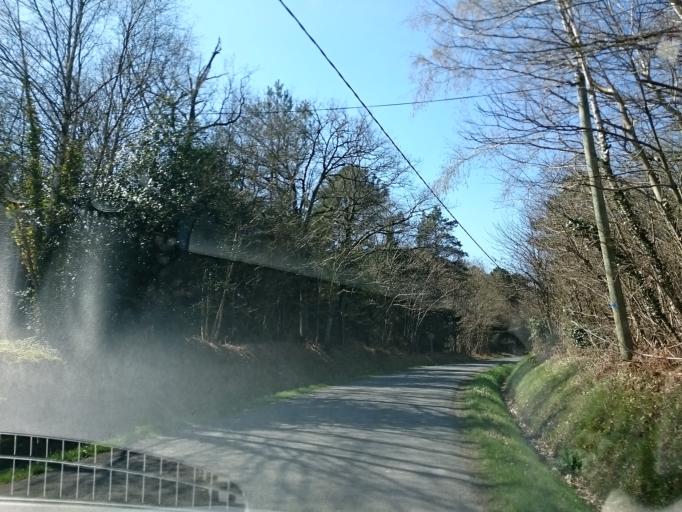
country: FR
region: Brittany
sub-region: Departement d'Ille-et-Vilaine
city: Crevin
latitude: 47.9572
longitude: -1.6642
